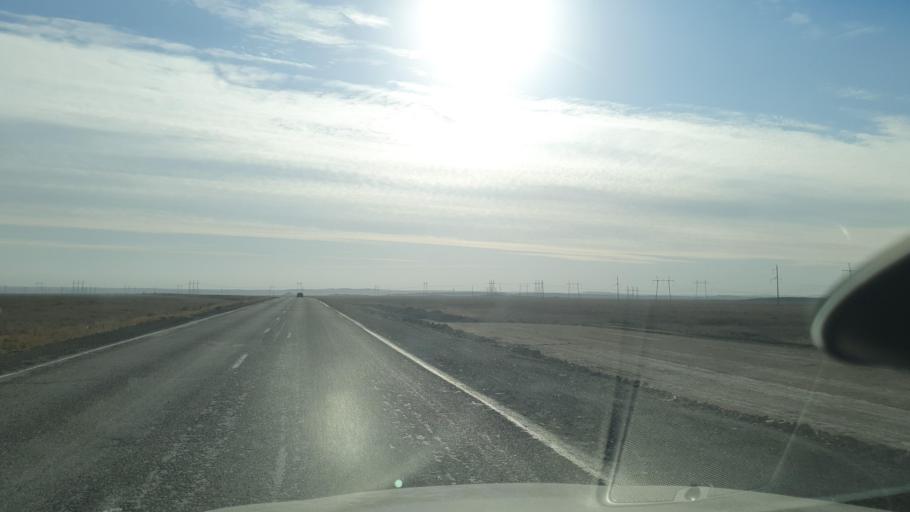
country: KZ
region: Zhambyl
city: Mynaral
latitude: 45.6169
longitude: 73.3959
